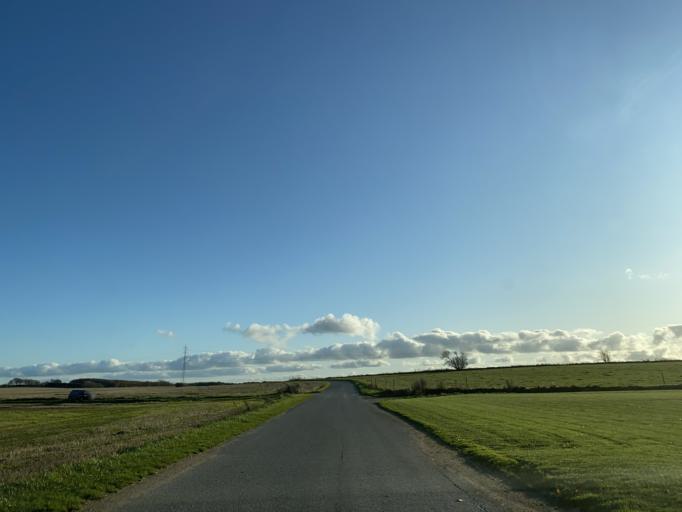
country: DK
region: Central Jutland
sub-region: Viborg Kommune
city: Bjerringbro
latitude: 56.3527
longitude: 9.7171
